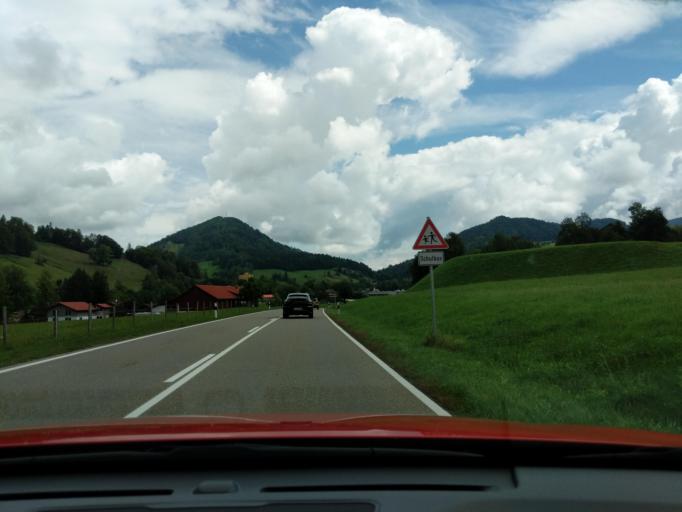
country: DE
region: Bavaria
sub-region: Swabia
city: Oberstaufen
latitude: 47.5396
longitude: 10.0076
